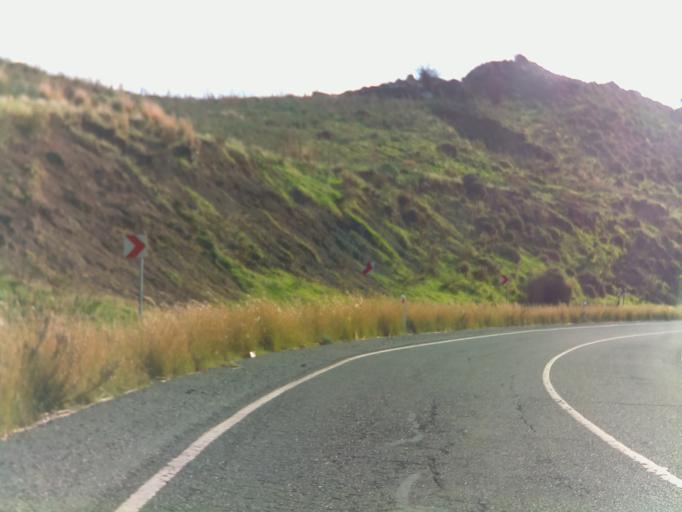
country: CY
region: Pafos
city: Mesogi
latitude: 34.7642
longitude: 32.5326
